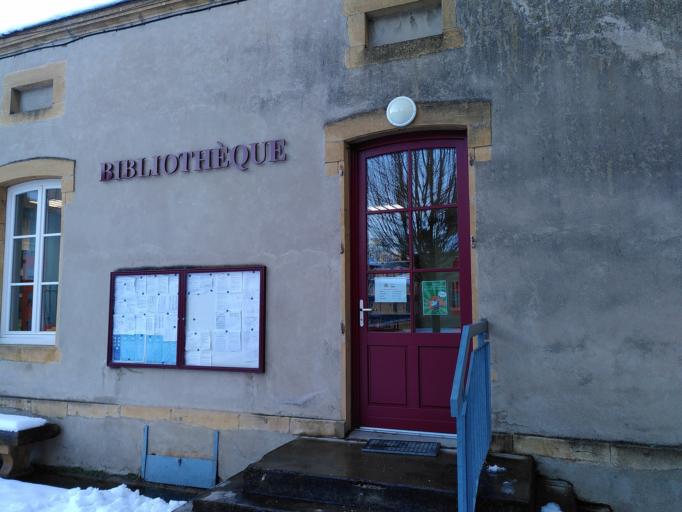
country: FR
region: Lorraine
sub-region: Departement de la Moselle
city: Ancy-sur-Moselle
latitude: 49.0567
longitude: 6.0582
